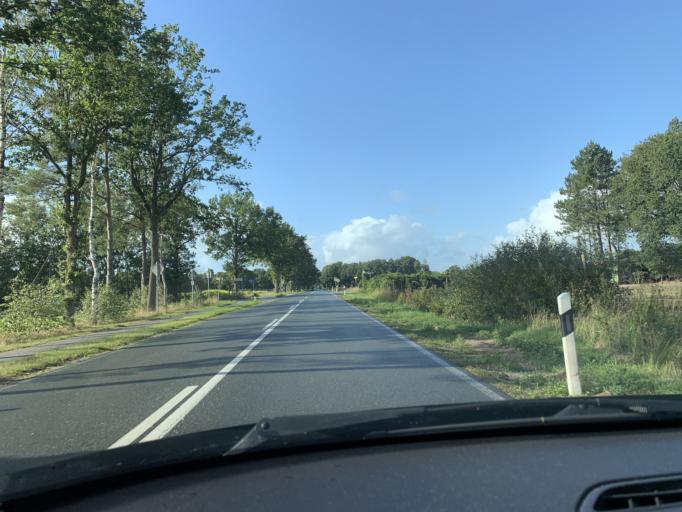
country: DE
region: Lower Saxony
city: Westerstede
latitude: 53.1901
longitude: 7.9213
